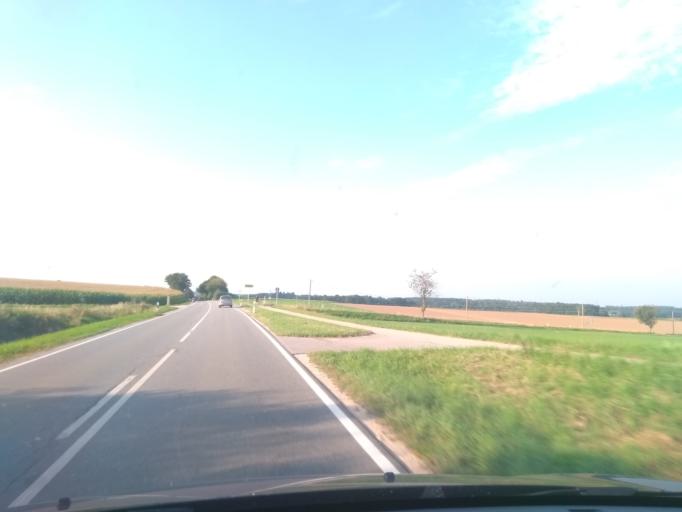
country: DE
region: Bavaria
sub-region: Upper Bavaria
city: Markt Indersdorf
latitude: 48.3352
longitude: 11.3886
